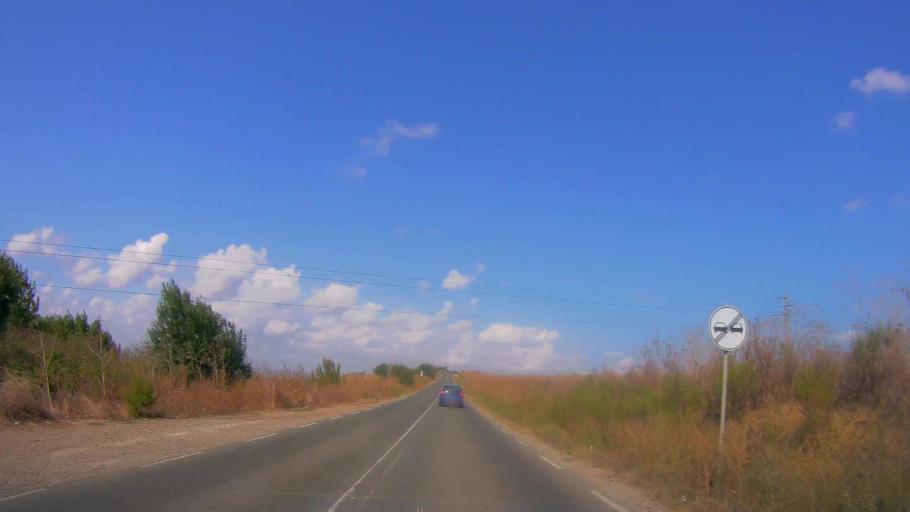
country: BG
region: Burgas
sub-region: Obshtina Burgas
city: Burgas
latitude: 42.4771
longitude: 27.3710
